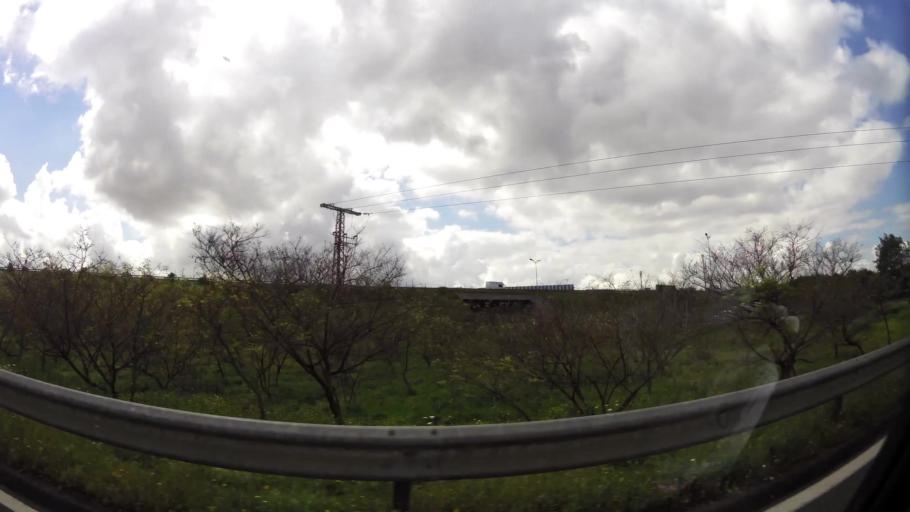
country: MA
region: Grand Casablanca
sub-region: Casablanca
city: Casablanca
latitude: 33.5294
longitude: -7.5664
